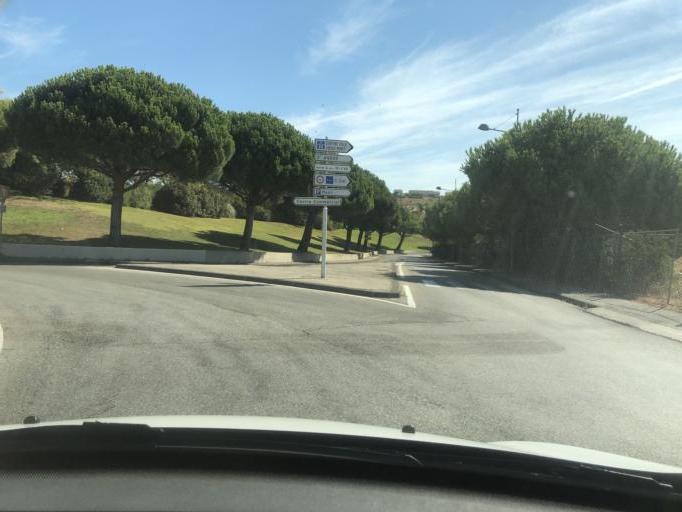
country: FR
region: Provence-Alpes-Cote d'Azur
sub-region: Departement des Bouches-du-Rhone
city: Marseille 15
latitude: 43.3617
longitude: 5.3498
